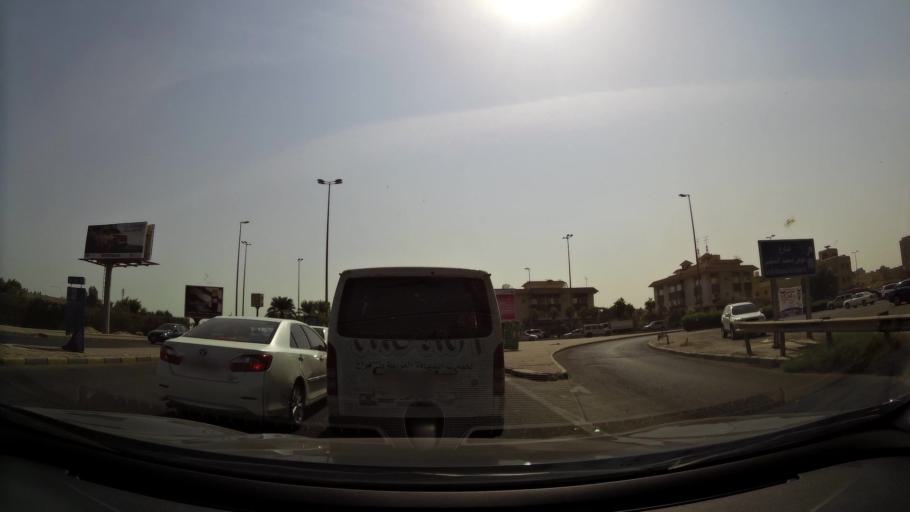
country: KW
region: Al Ahmadi
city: Al Manqaf
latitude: 29.0927
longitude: 48.1375
